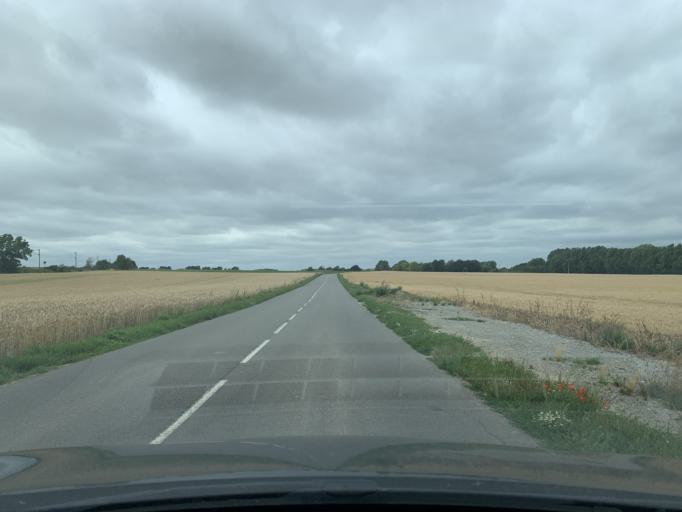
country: FR
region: Nord-Pas-de-Calais
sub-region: Departement du Nord
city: Aubigny-au-Bac
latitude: 50.2541
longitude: 3.1786
